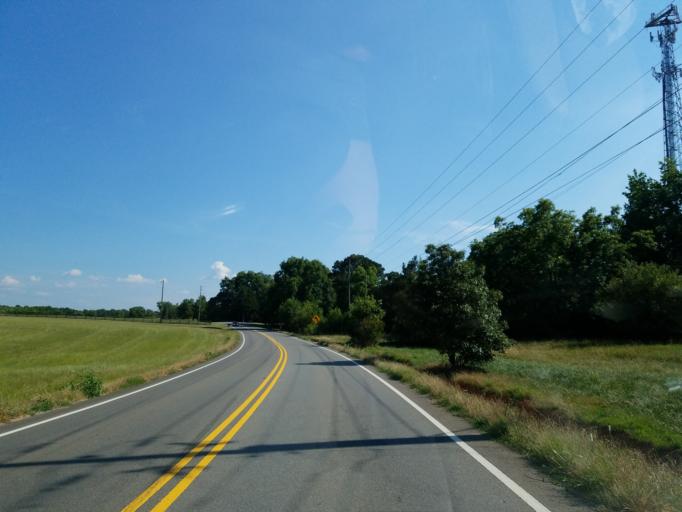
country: US
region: Georgia
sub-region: Fulton County
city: Milton
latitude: 34.2352
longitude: -84.2909
